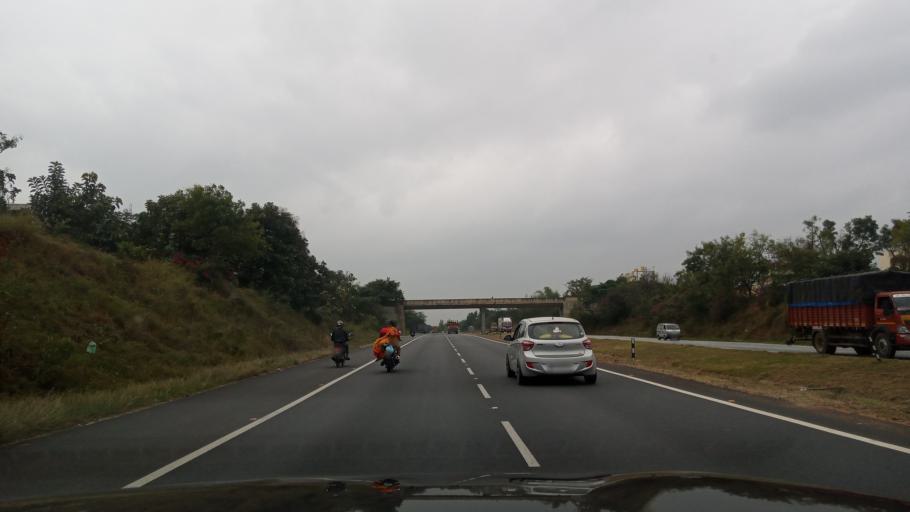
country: IN
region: Karnataka
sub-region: Bangalore Rural
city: Nelamangala
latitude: 13.0108
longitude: 77.4755
